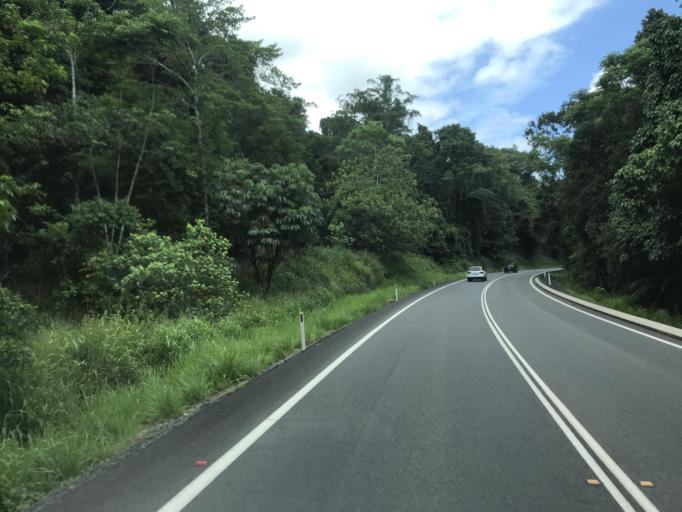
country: AU
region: Queensland
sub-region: Cassowary Coast
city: Innisfail
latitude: -17.6077
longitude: 145.7764
